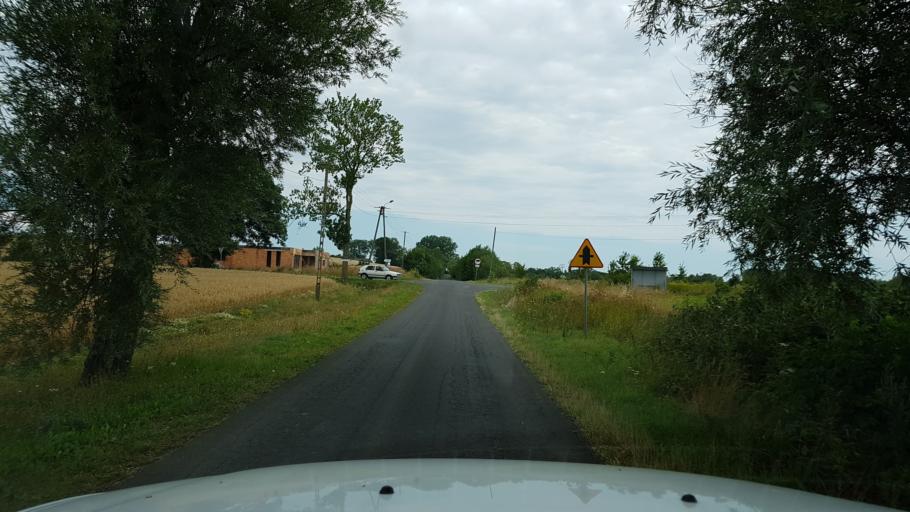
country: PL
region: West Pomeranian Voivodeship
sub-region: Powiat koszalinski
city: Mielno
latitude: 54.1712
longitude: 16.0354
